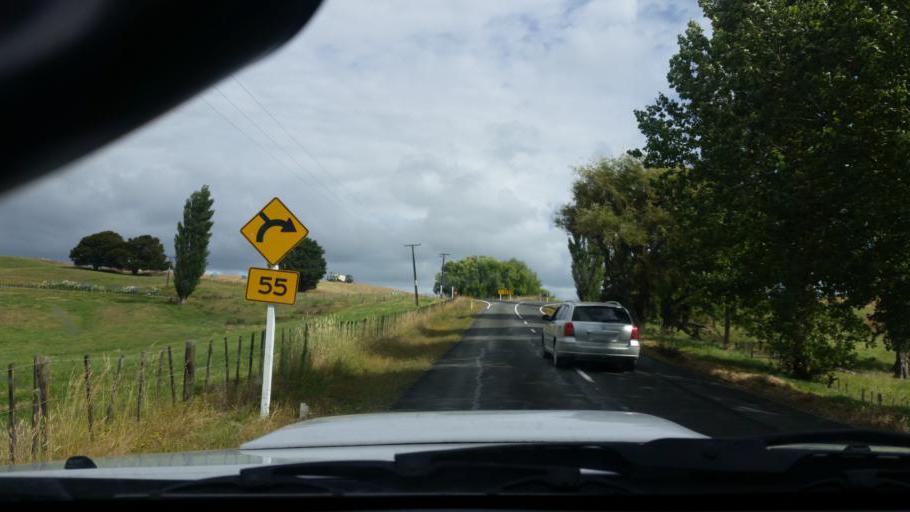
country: NZ
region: Auckland
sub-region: Auckland
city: Wellsford
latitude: -36.1298
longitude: 174.3580
